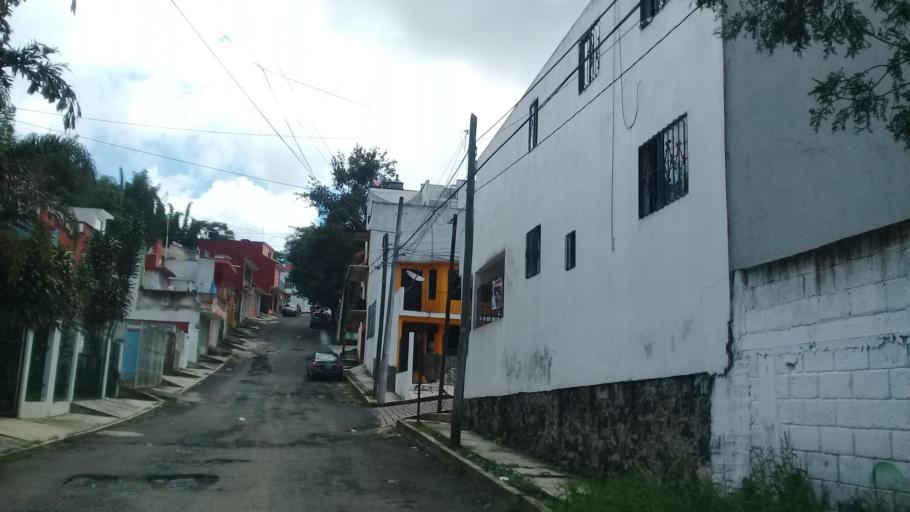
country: MX
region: Veracruz
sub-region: Xalapa
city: Xalapa de Enriquez
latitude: 19.5056
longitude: -96.9277
